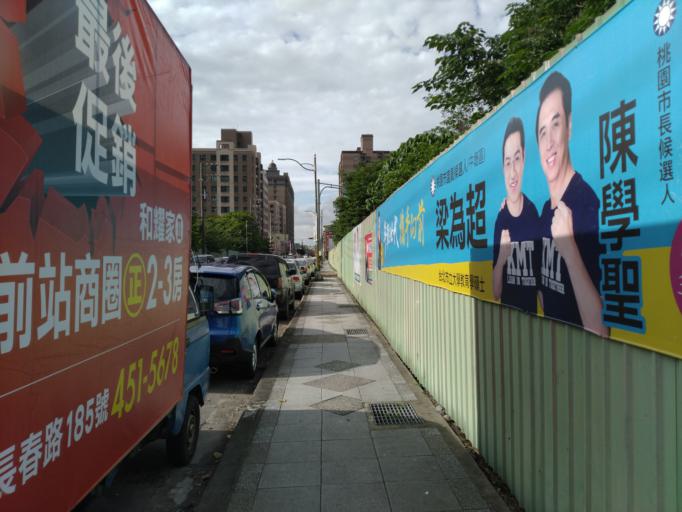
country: TW
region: Taiwan
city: Taoyuan City
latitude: 24.9761
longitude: 121.2527
